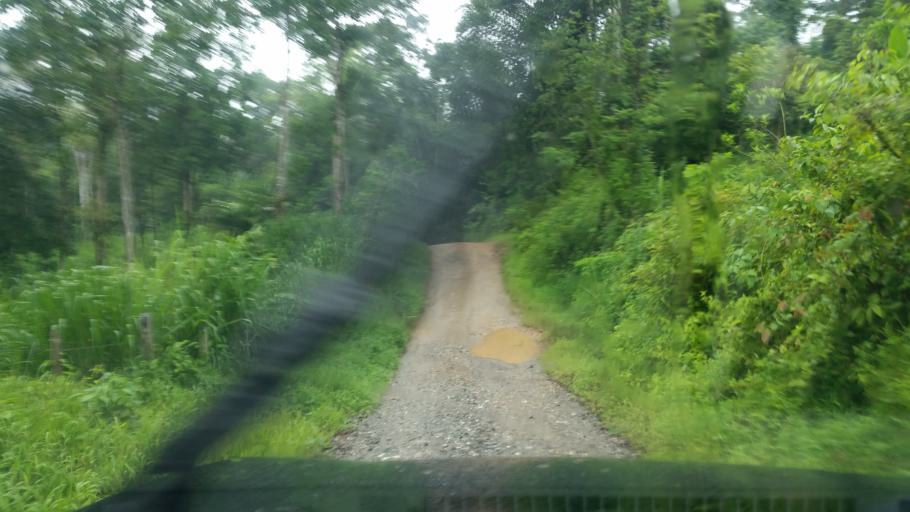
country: NI
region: Atlantico Norte (RAAN)
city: Bonanza
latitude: 14.0796
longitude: -84.6704
